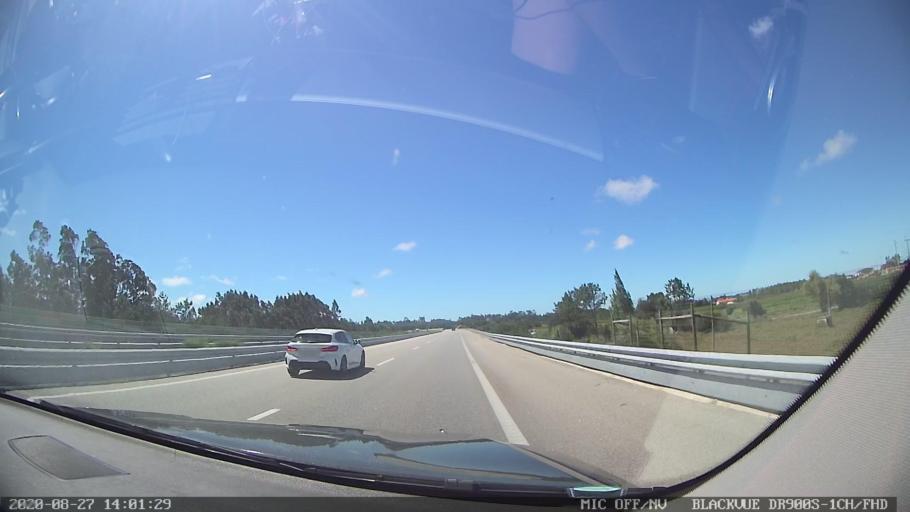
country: PT
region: Coimbra
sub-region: Figueira da Foz
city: Alhadas
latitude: 40.2516
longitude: -8.7713
